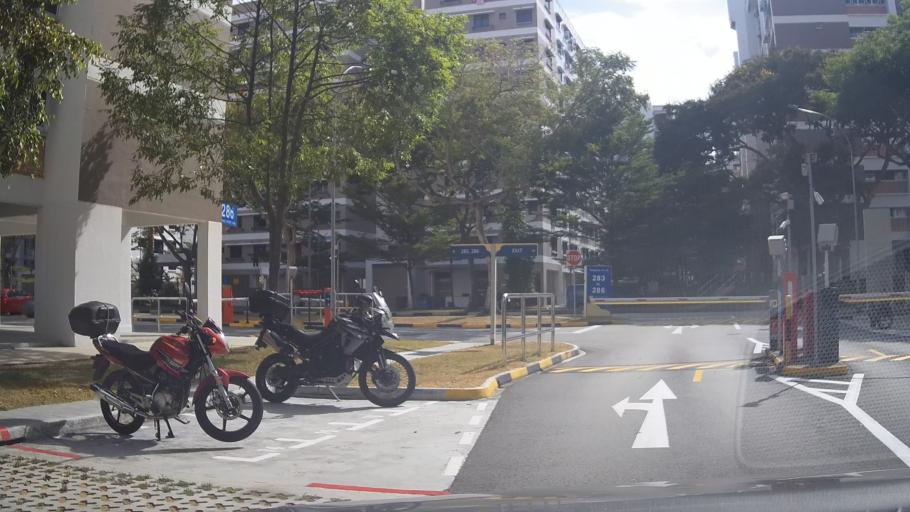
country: SG
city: Singapore
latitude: 1.3492
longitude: 103.9533
